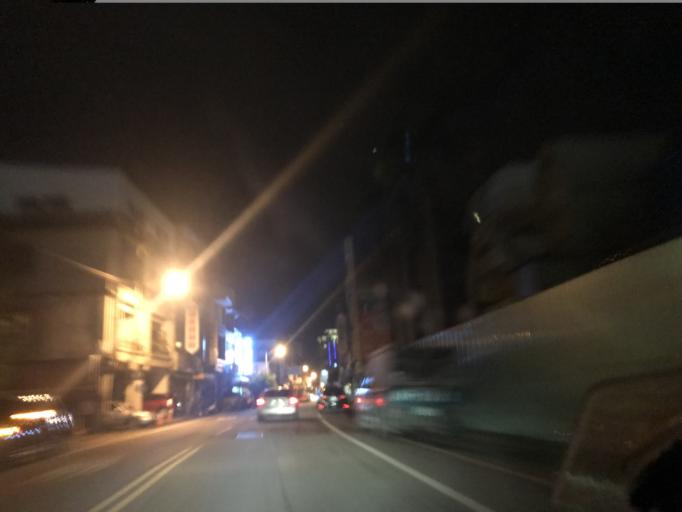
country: TW
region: Taiwan
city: Daxi
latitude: 24.8641
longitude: 121.2144
